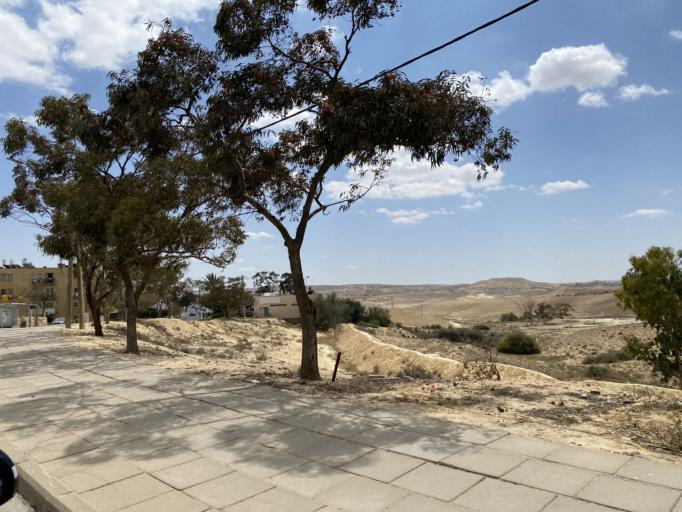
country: IL
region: Southern District
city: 'Arad
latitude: 31.2553
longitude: 35.2146
